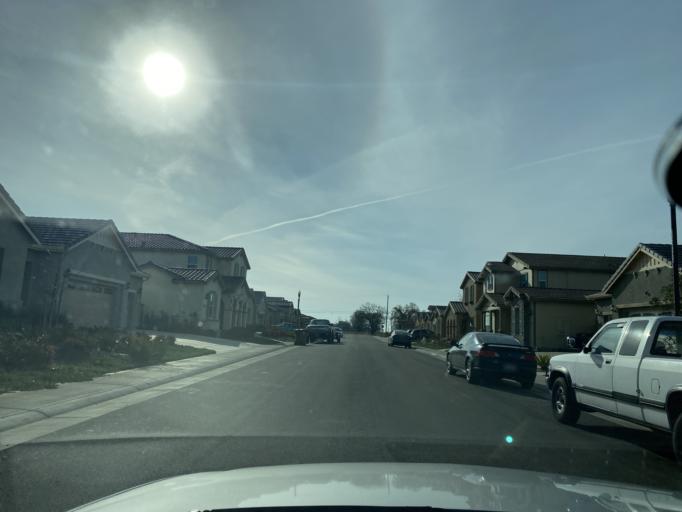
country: US
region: California
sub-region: Sacramento County
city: Elk Grove
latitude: 38.3922
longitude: -121.3867
